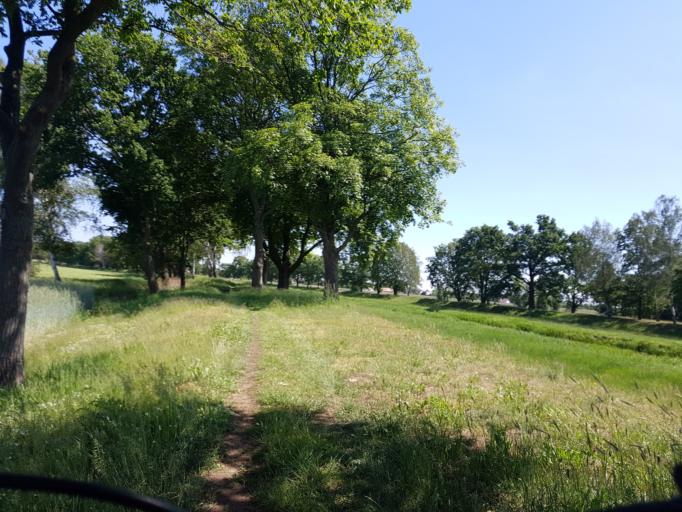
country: DE
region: Brandenburg
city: Elsterwerda
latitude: 51.4556
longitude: 13.4979
